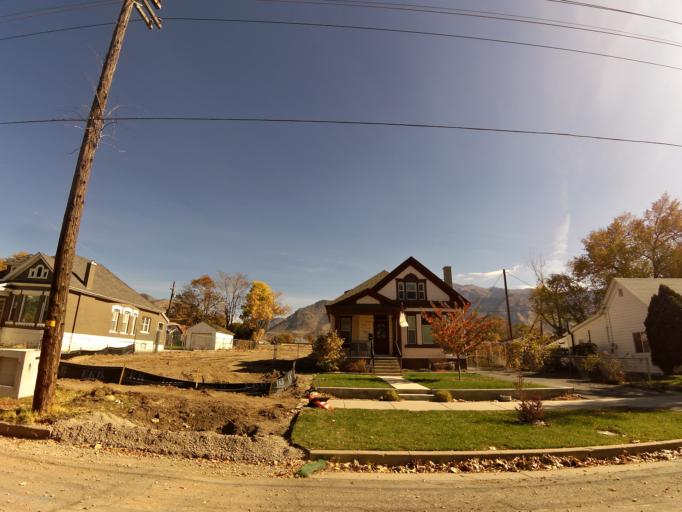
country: US
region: Utah
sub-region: Weber County
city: Ogden
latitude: 41.2276
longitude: -111.9675
